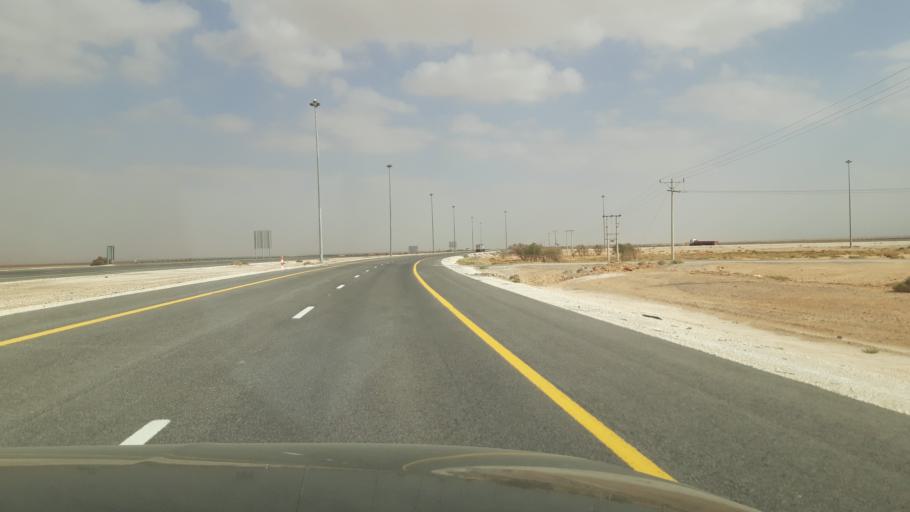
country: JO
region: Amman
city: Al Azraq ash Shamali
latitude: 31.7815
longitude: 36.7923
